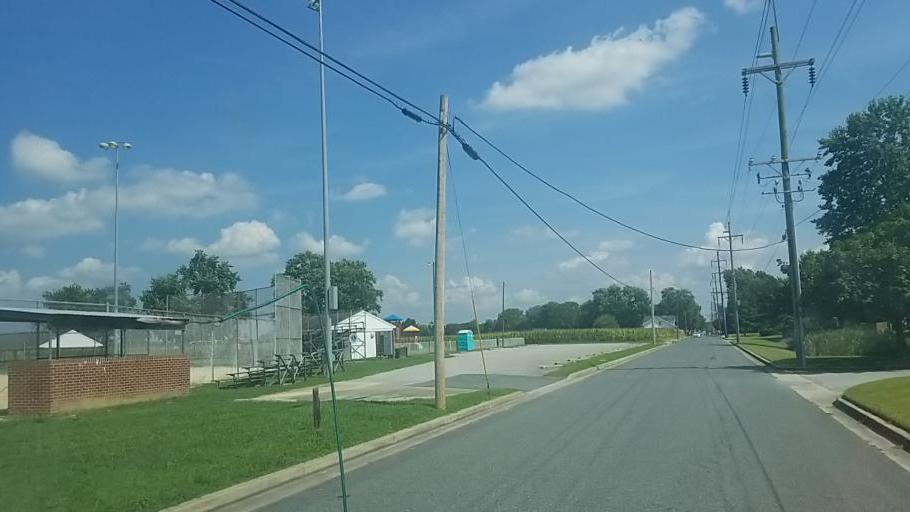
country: US
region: Maryland
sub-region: Wicomico County
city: Hebron
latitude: 38.4221
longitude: -75.6930
